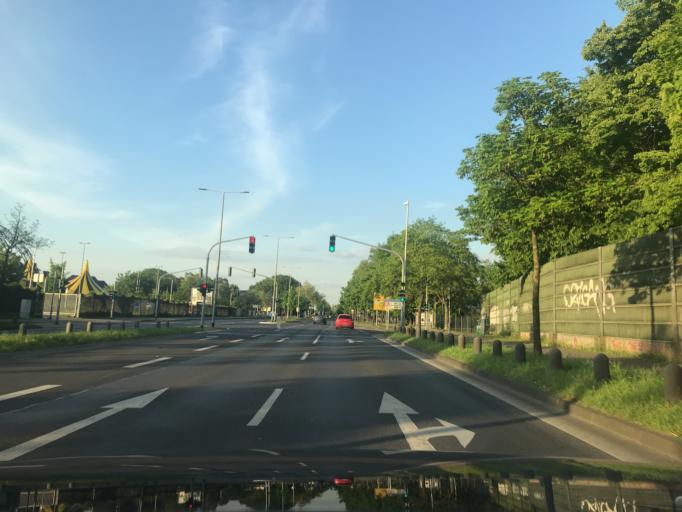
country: DE
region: North Rhine-Westphalia
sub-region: Regierungsbezirk Dusseldorf
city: Monchengladbach
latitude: 51.1683
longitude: 6.3862
